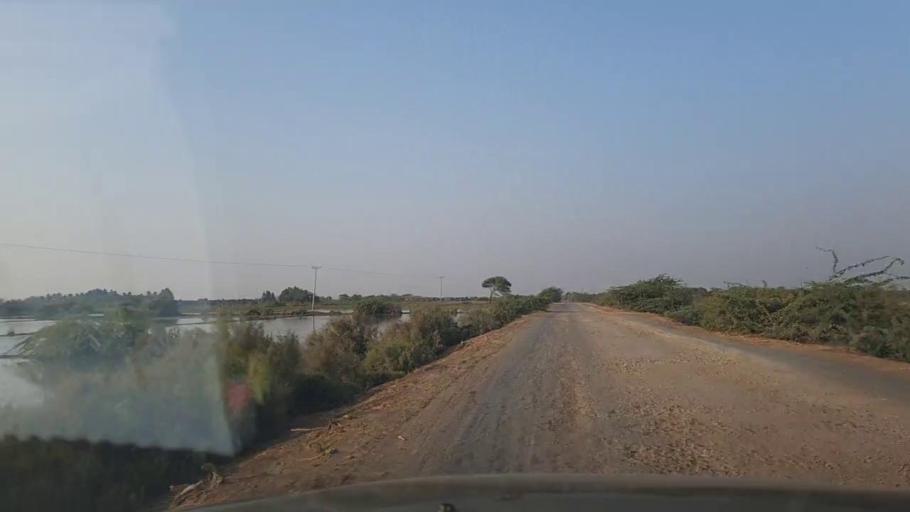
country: PK
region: Sindh
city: Keti Bandar
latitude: 24.2782
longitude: 67.5876
